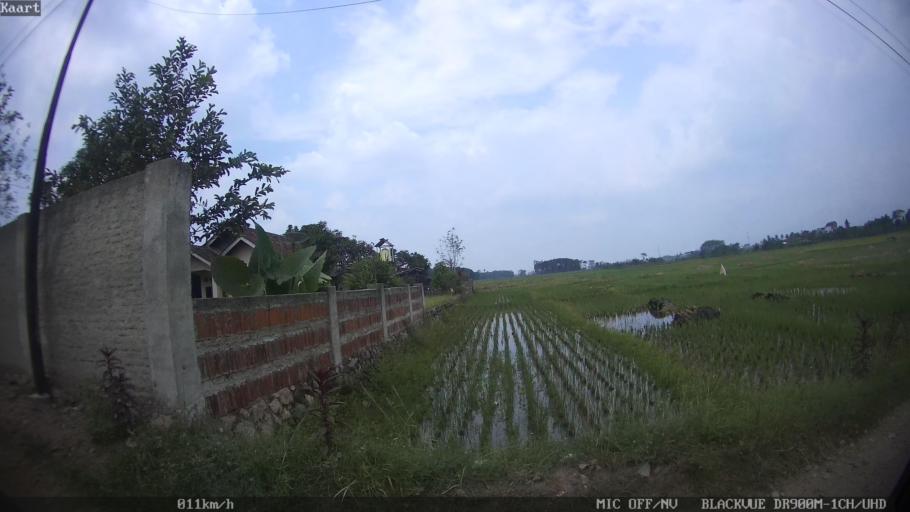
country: ID
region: Lampung
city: Gadingrejo
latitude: -5.3727
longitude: 105.0286
